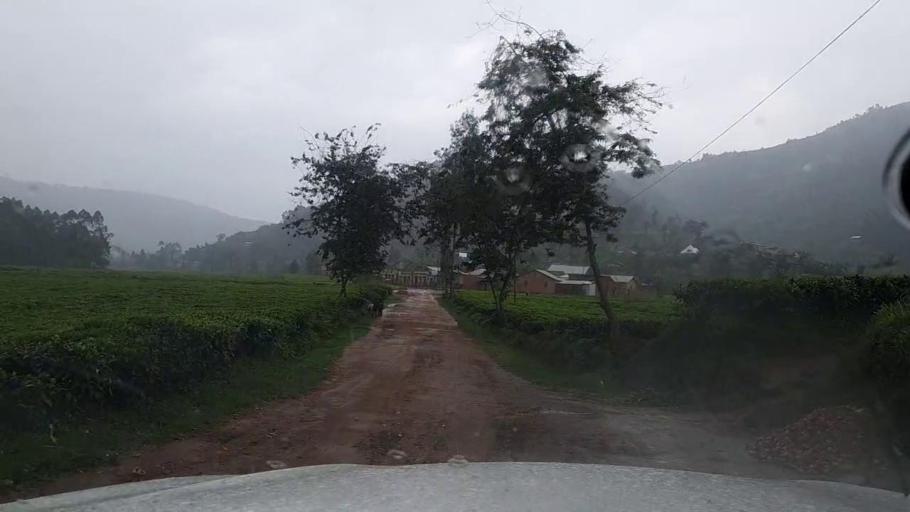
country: RW
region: Northern Province
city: Byumba
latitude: -1.6519
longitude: 29.9212
